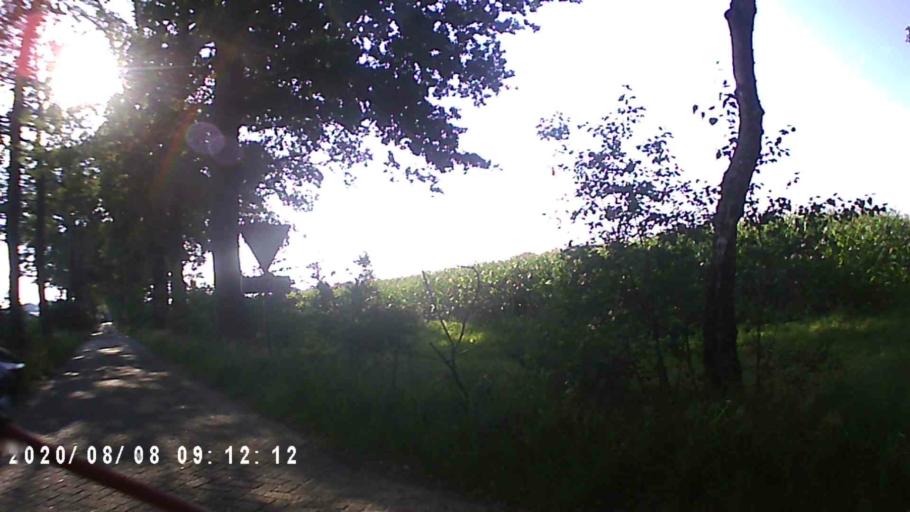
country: NL
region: Groningen
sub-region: Gemeente Leek
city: Leek
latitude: 53.0523
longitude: 6.3292
